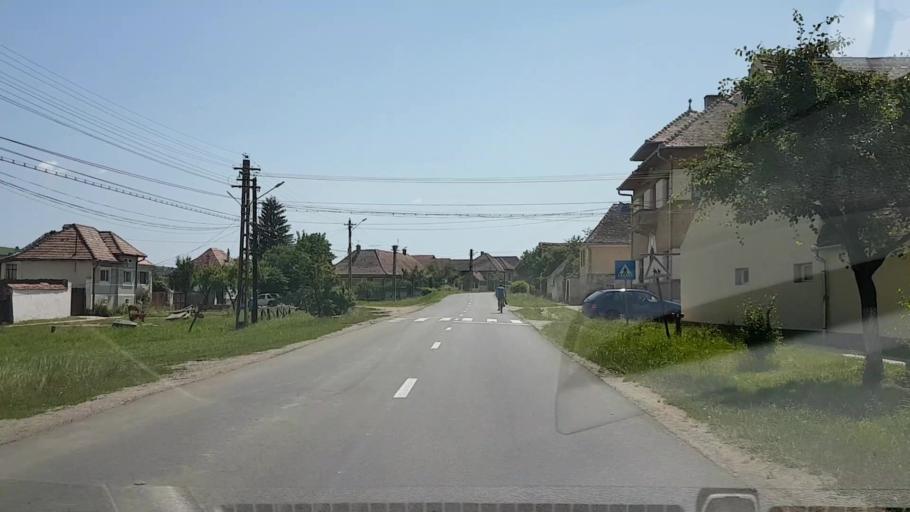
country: RO
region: Sibiu
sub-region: Comuna Merghindeal
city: Merghindeal
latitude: 45.9649
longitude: 24.7307
